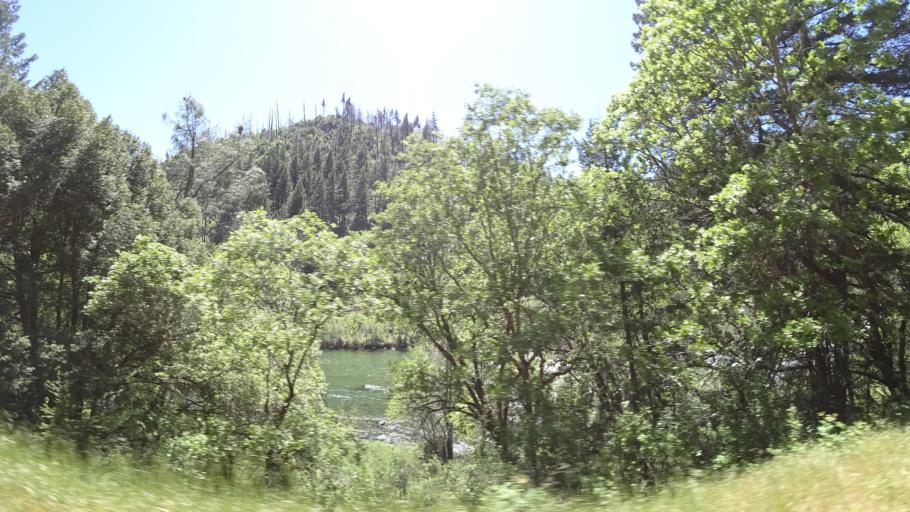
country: US
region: California
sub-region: Trinity County
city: Hayfork
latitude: 40.7493
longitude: -123.2746
